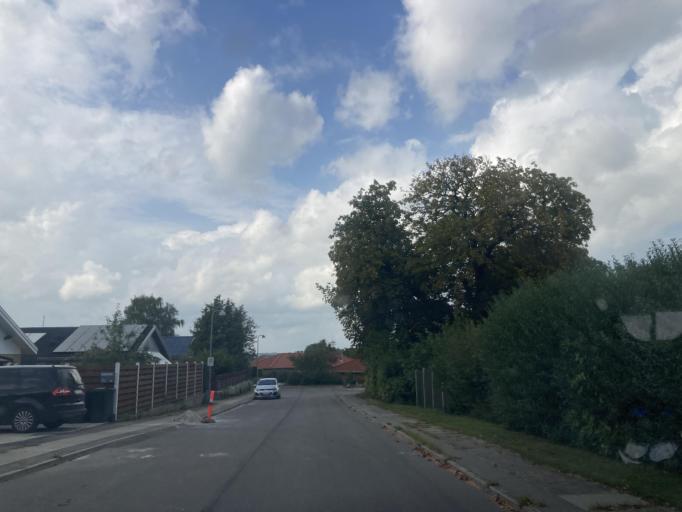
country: DK
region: Zealand
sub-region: Roskilde Kommune
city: Svogerslev
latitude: 55.5973
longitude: 12.0128
